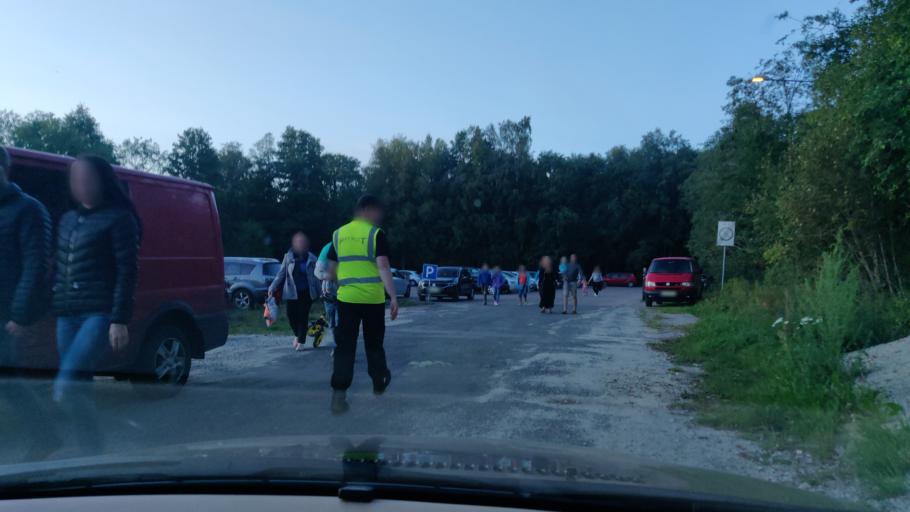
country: EE
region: Harju
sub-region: Keila linn
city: Keila
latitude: 59.3469
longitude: 24.2490
